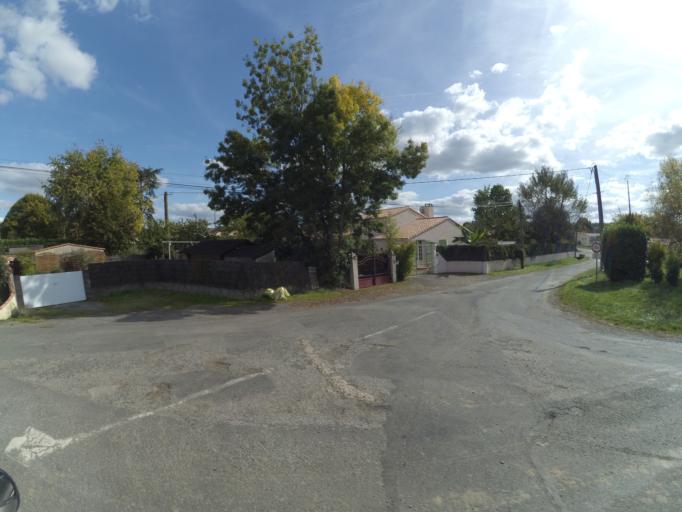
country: FR
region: Pays de la Loire
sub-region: Departement de la Loire-Atlantique
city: Le Pallet
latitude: 47.1534
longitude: -1.3445
